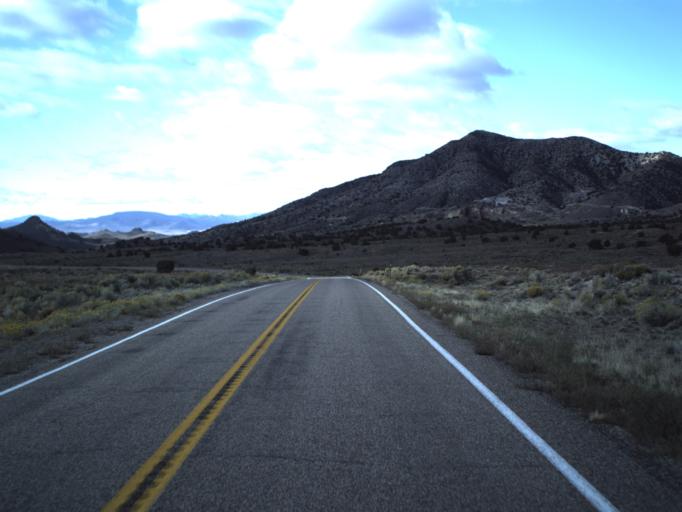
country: US
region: Utah
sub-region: Beaver County
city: Milford
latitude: 38.4580
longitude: -113.2561
